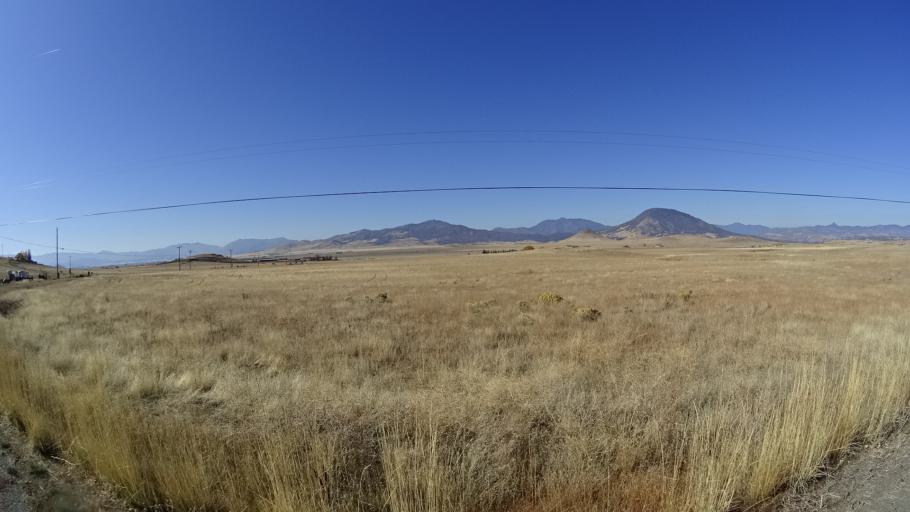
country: US
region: California
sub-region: Siskiyou County
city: Montague
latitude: 41.7954
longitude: -122.4172
